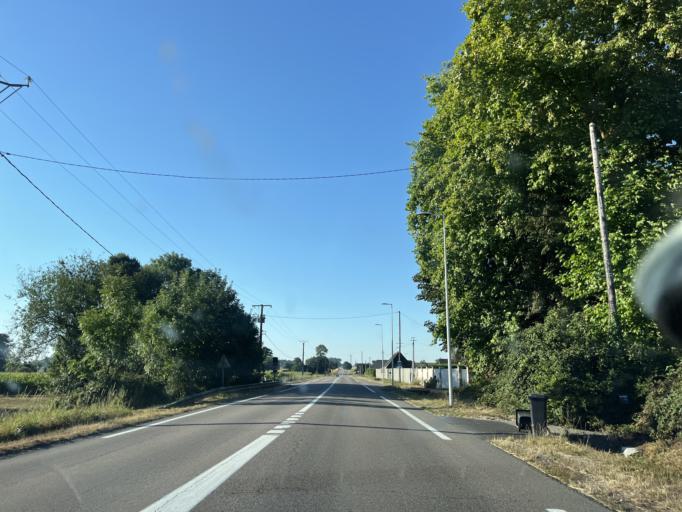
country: FR
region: Haute-Normandie
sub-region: Departement de la Seine-Maritime
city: Fauville-en-Caux
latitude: 49.5942
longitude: 0.5955
